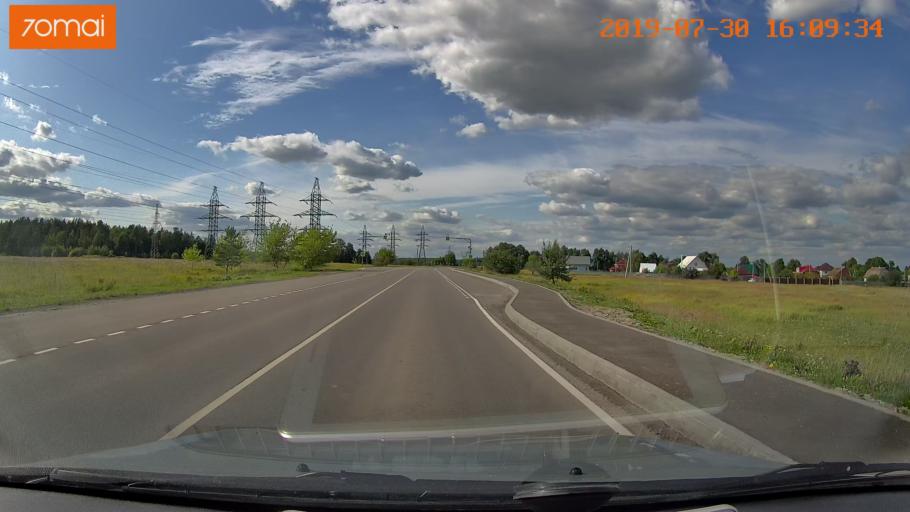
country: RU
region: Moskovskaya
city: Peski
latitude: 55.2542
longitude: 38.7180
